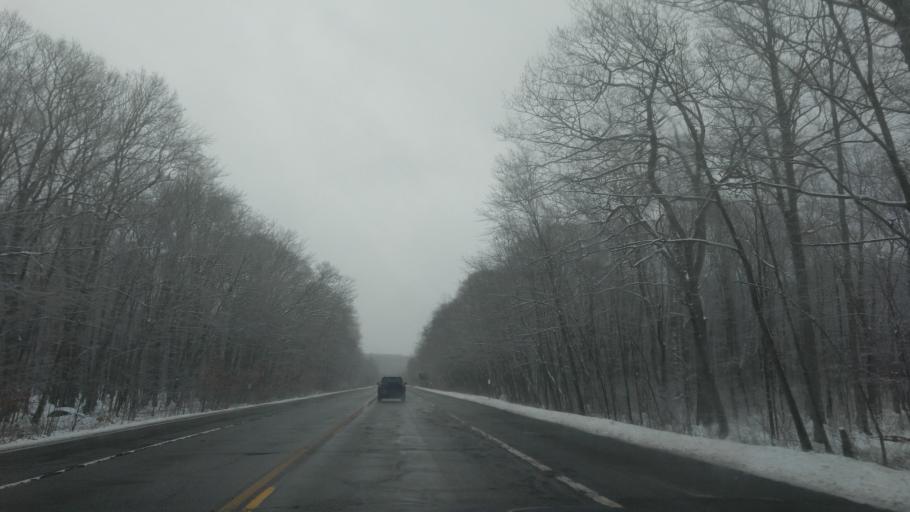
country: US
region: Rhode Island
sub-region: Providence County
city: North Scituate
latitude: 41.8317
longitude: -71.6527
